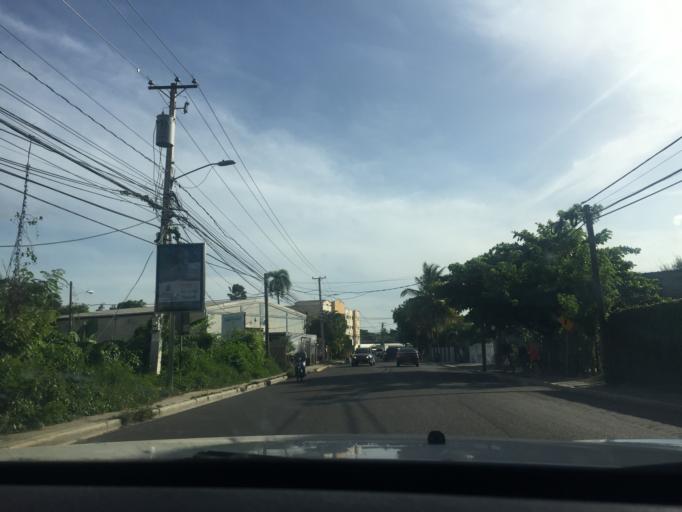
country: DO
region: Santiago
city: Tamboril
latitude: 19.4689
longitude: -70.6540
